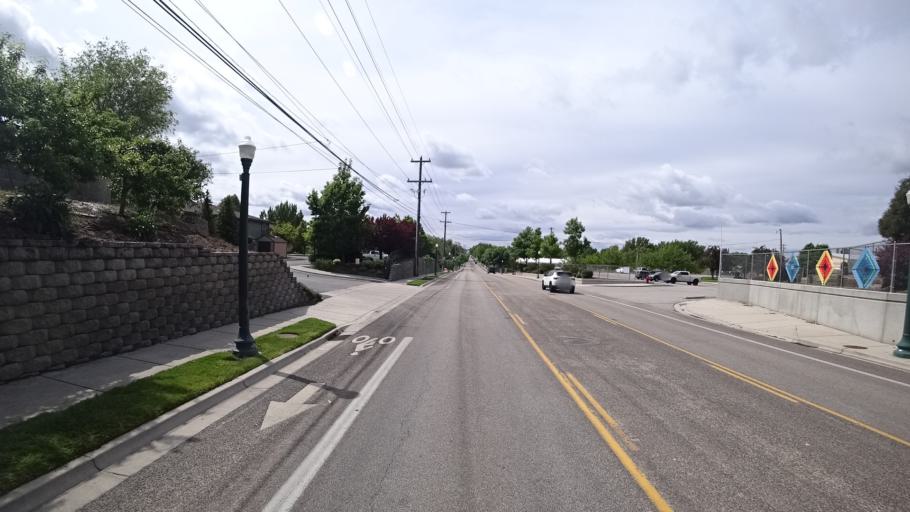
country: US
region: Idaho
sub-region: Ada County
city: Eagle
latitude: 43.7002
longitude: -116.3540
